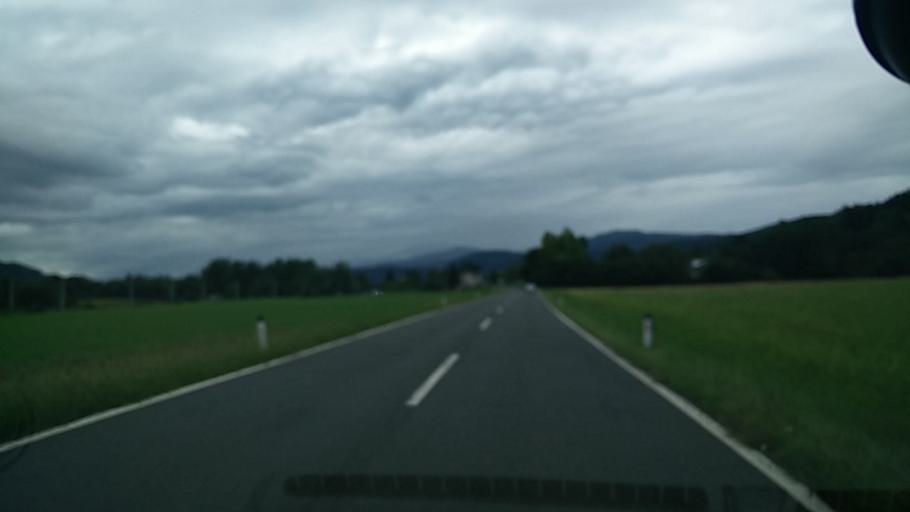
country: AT
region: Carinthia
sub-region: Politischer Bezirk Klagenfurt Land
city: Maria Worth
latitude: 46.6220
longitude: 14.1857
